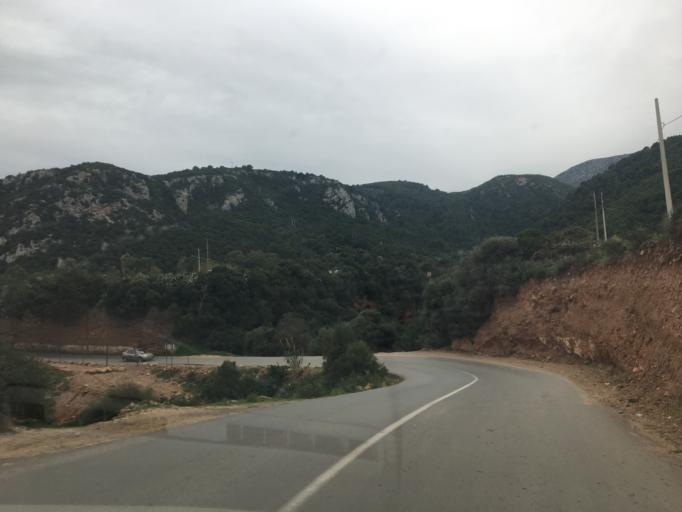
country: DZ
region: Tipaza
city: Tipasa
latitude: 36.6260
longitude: 2.4040
